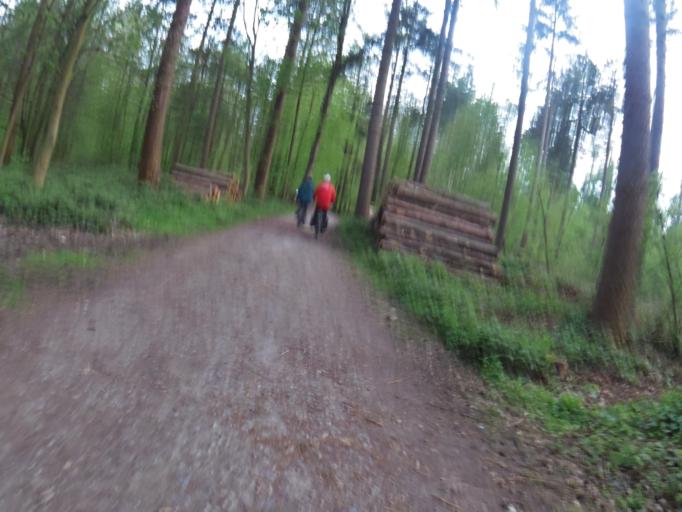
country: BE
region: Flanders
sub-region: Provincie Vlaams-Brabant
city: Wezembeek-Oppem
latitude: 50.8226
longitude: 4.4682
